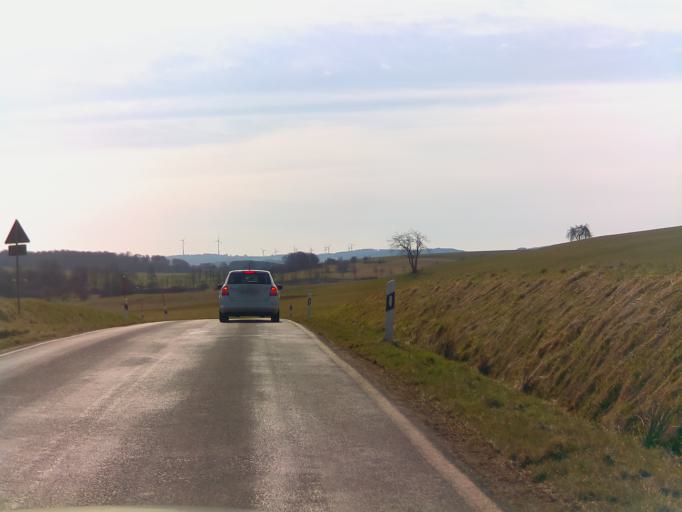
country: DE
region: Hesse
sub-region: Regierungsbezirk Giessen
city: Grunberg
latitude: 50.6256
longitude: 9.0688
